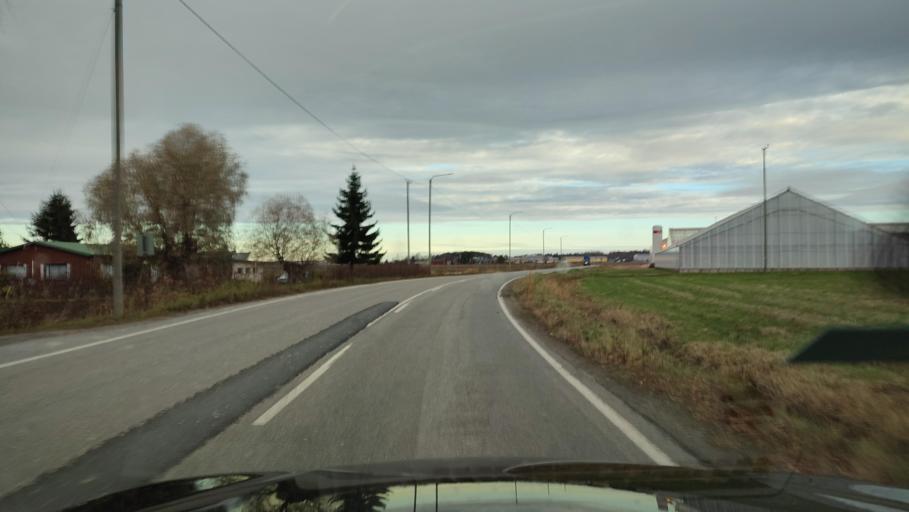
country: FI
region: Ostrobothnia
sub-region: Sydosterbotten
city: Naerpes
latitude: 62.4321
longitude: 21.3479
